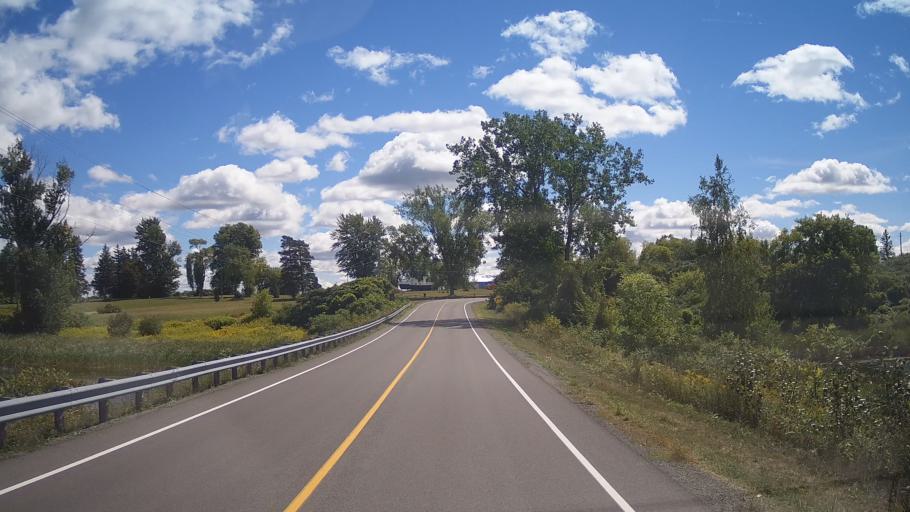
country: US
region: New York
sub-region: St. Lawrence County
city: Ogdensburg
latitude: 44.8354
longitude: -75.3150
